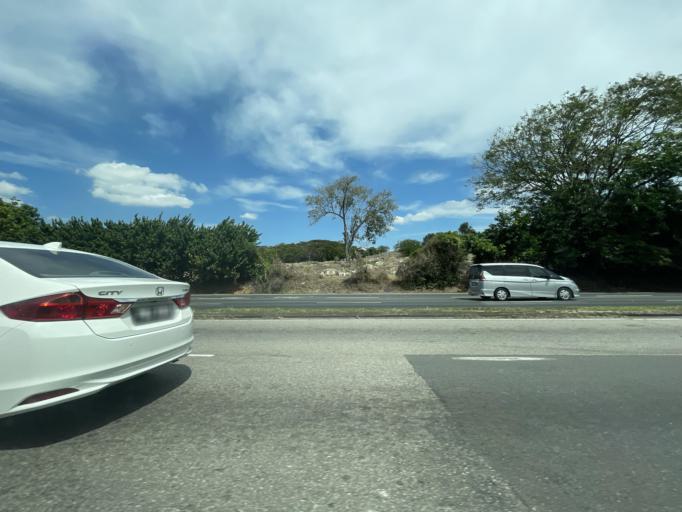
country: MY
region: Melaka
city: Batu Berendam
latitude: 2.2418
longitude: 102.2235
